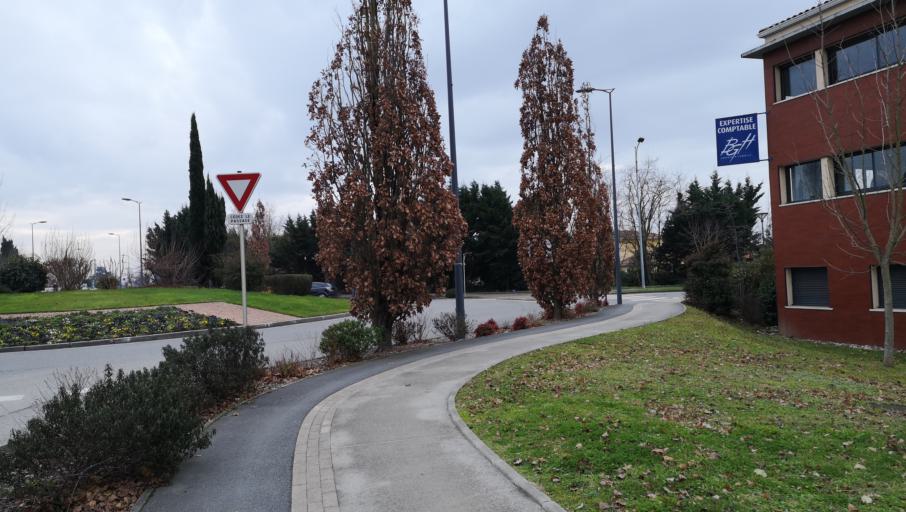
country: FR
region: Midi-Pyrenees
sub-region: Departement de la Haute-Garonne
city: Beauzelle
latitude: 43.6504
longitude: 1.3814
